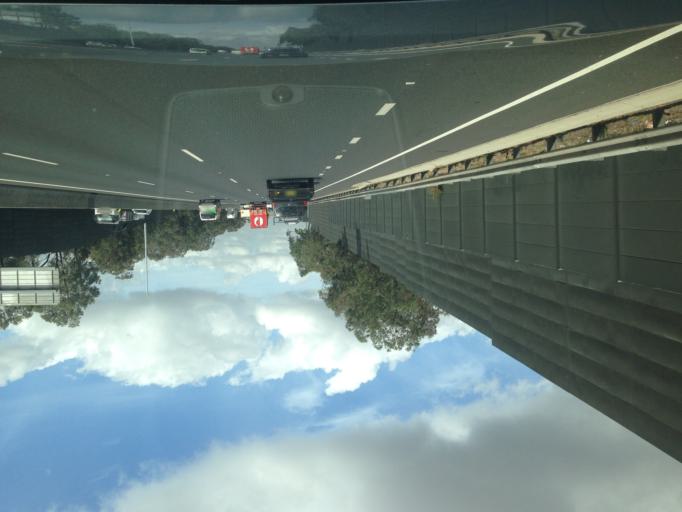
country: AU
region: New South Wales
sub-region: Bankstown
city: Revesby
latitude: -33.9404
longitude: 151.0134
